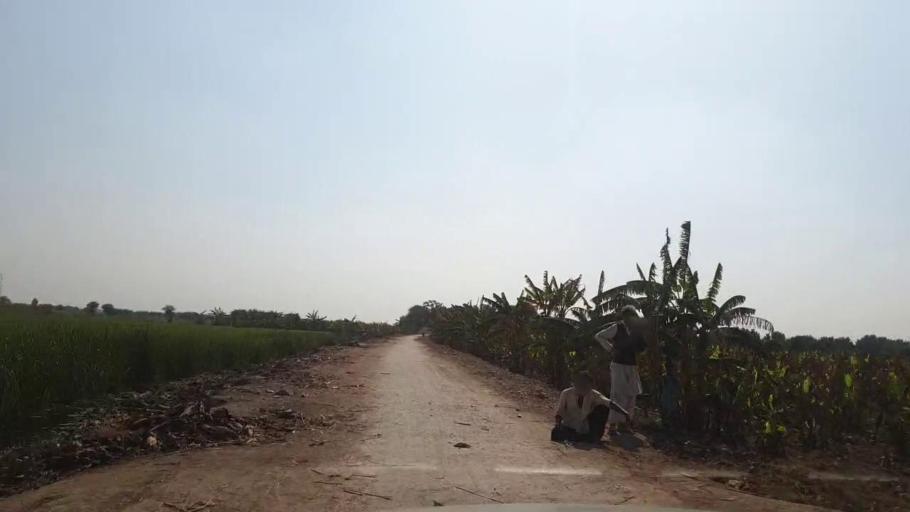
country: PK
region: Sindh
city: Tando Allahyar
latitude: 25.5501
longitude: 68.6982
